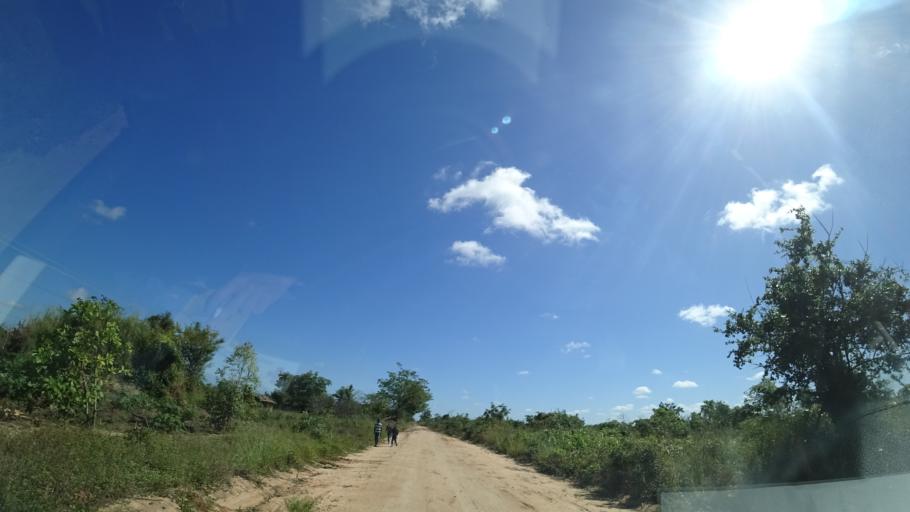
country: MZ
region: Sofala
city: Dondo
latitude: -19.2852
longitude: 34.6861
